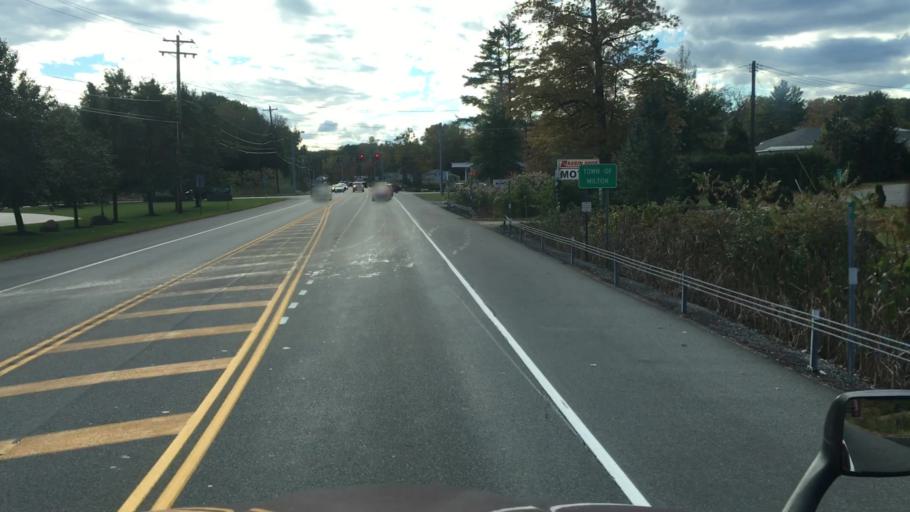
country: US
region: New York
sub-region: Saratoga County
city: North Ballston Spa
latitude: 43.0238
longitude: -73.8379
